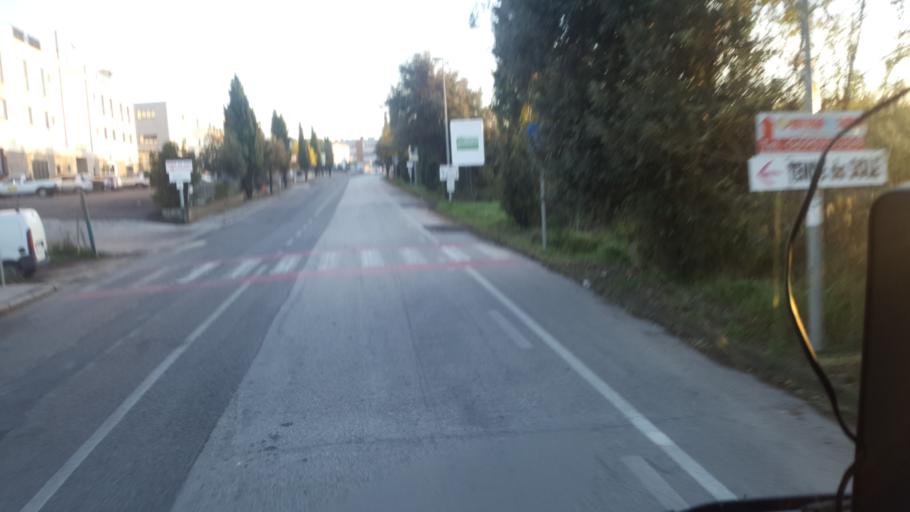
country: IT
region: Latium
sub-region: Citta metropolitana di Roma Capitale
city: Formello
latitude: 42.0486
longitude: 12.3990
